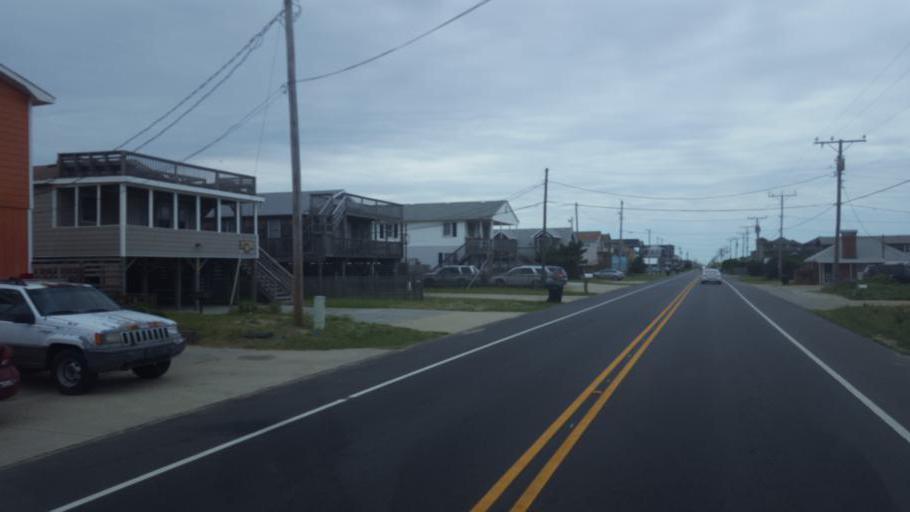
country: US
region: North Carolina
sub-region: Dare County
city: Kill Devil Hills
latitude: 36.0036
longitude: -75.6510
